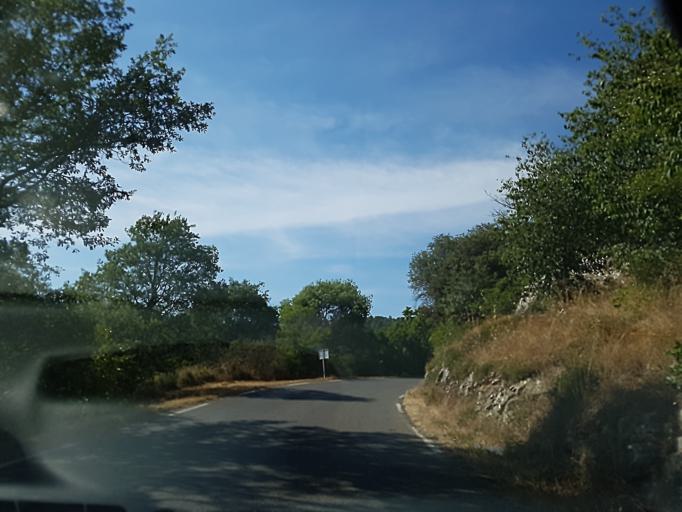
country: FR
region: Provence-Alpes-Cote d'Azur
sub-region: Departement du Var
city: Bras
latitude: 43.4685
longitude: 5.9470
